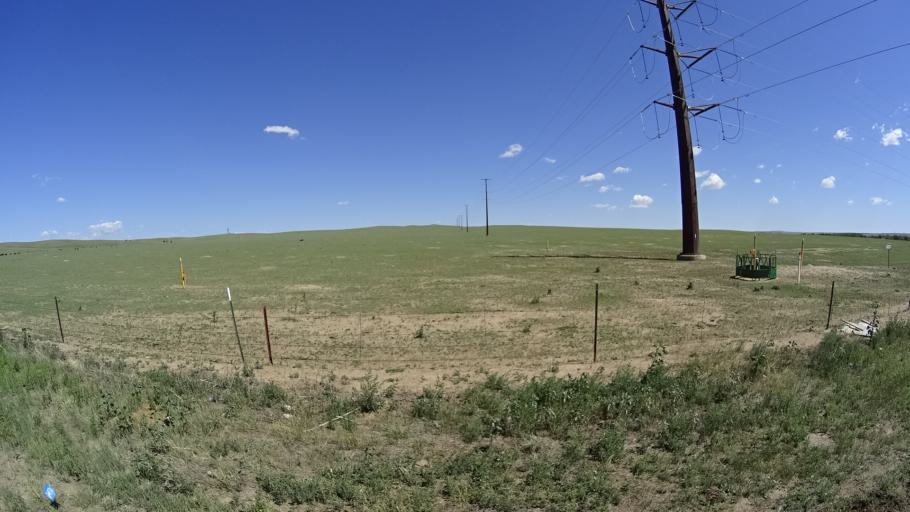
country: US
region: Colorado
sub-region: El Paso County
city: Security-Widefield
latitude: 38.7813
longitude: -104.6648
